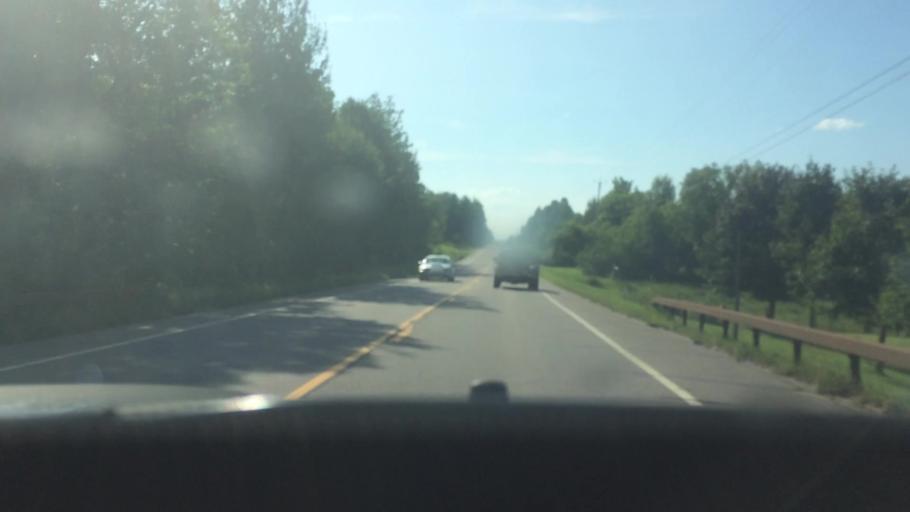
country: US
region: New York
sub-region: Franklin County
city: Malone
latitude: 44.8575
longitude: -74.2314
